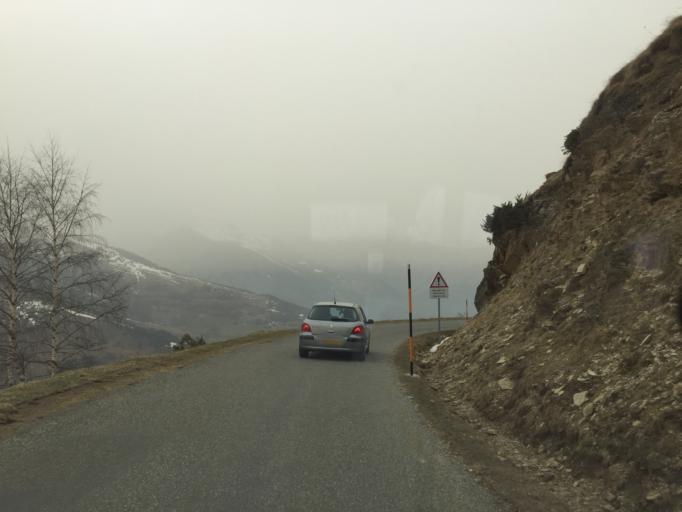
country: FR
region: Midi-Pyrenees
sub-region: Departement des Hautes-Pyrenees
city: Saint-Lary-Soulan
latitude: 42.8007
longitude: 0.3709
